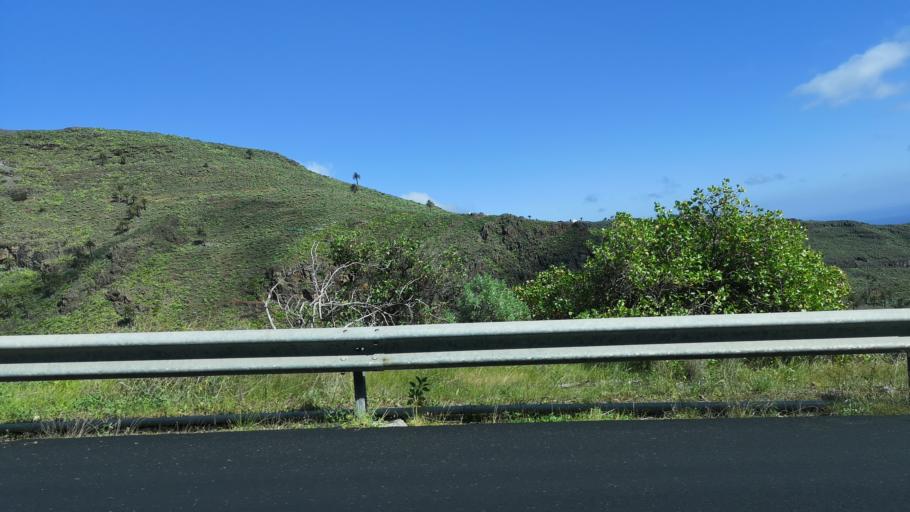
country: ES
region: Canary Islands
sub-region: Provincia de Santa Cruz de Tenerife
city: Alajero
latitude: 28.0692
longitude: -17.2067
